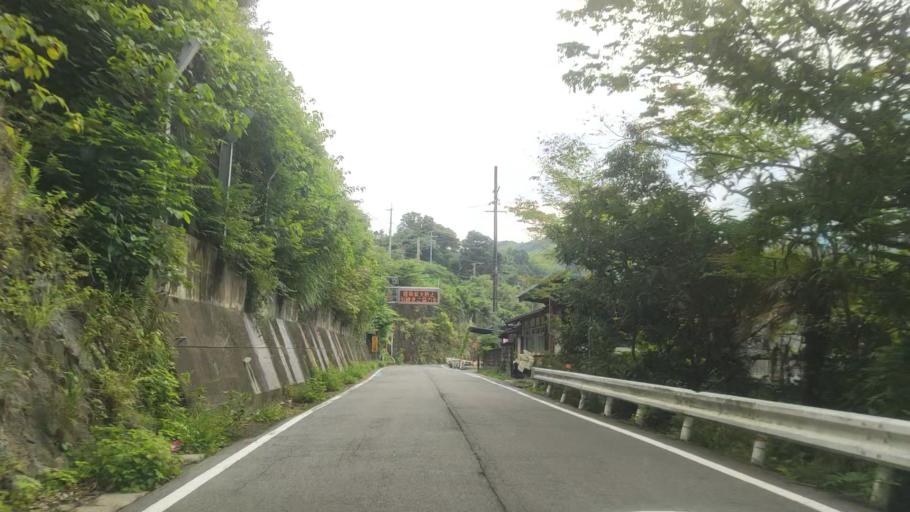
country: JP
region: Wakayama
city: Hashimoto
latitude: 34.2879
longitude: 135.5640
